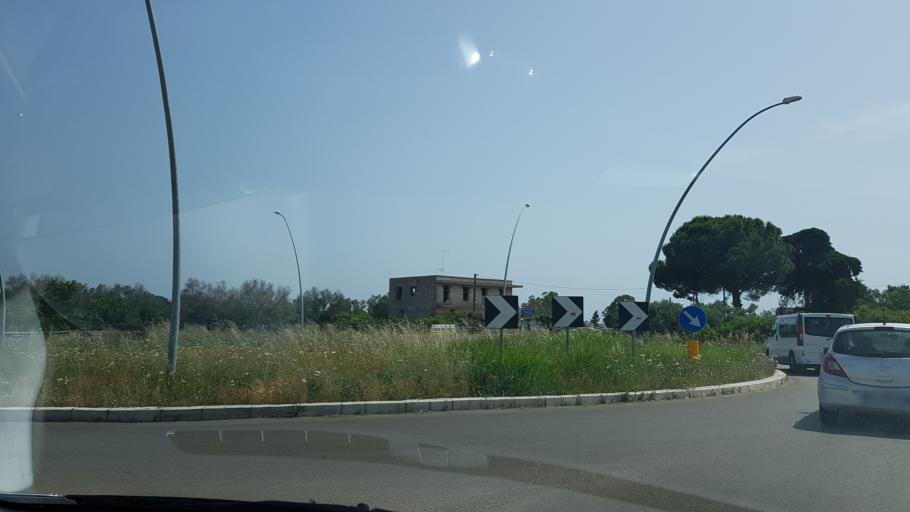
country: IT
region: Apulia
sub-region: Provincia di Lecce
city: Porto Cesareo
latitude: 40.3029
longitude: 17.8599
